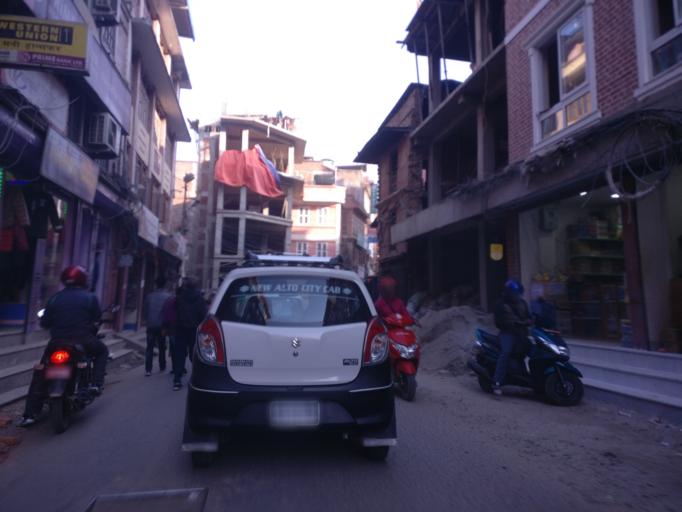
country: NP
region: Central Region
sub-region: Bagmati Zone
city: Patan
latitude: 27.6736
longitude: 85.3237
